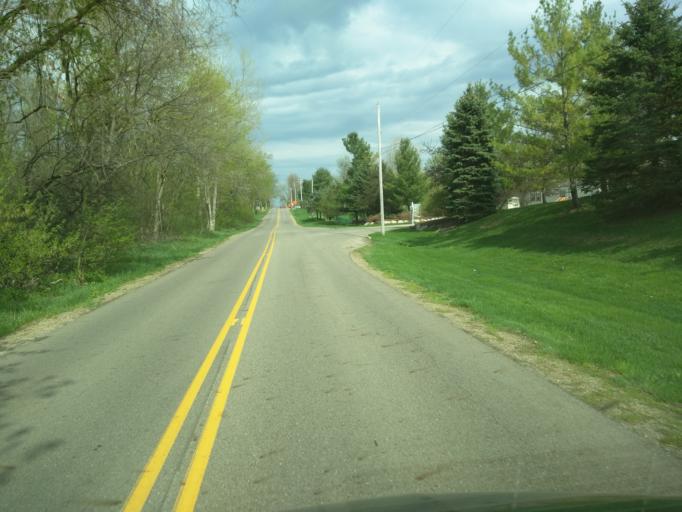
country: US
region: Michigan
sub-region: Eaton County
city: Dimondale
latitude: 42.6831
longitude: -84.6125
